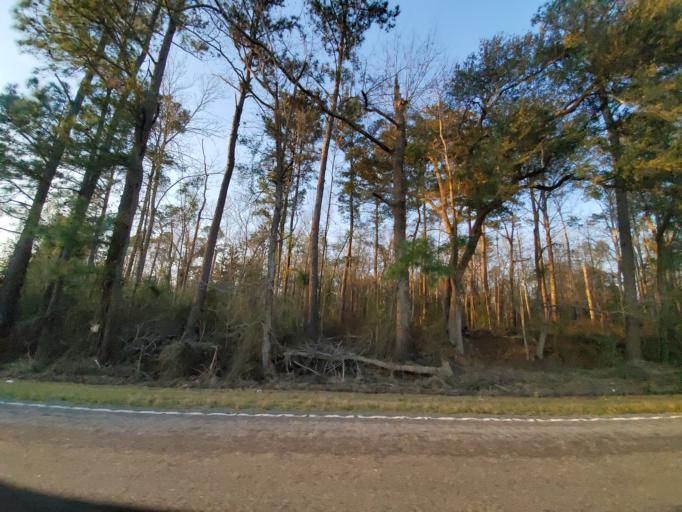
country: US
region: South Carolina
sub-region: Dorchester County
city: Saint George
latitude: 33.0465
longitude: -80.5756
